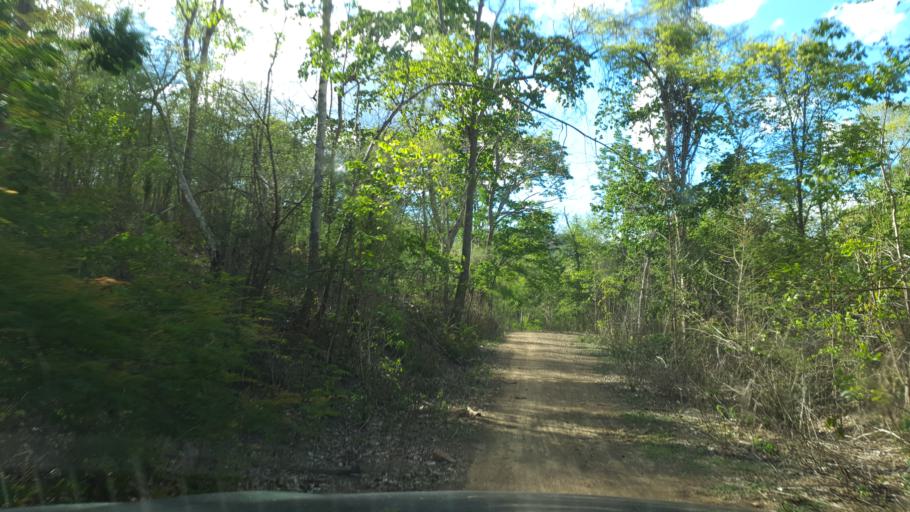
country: TH
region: Lampang
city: Sop Prap
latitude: 17.8438
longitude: 99.2861
